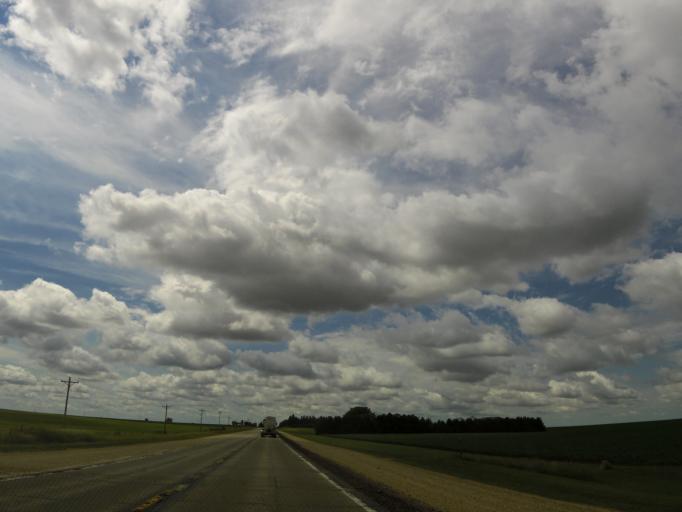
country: US
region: Iowa
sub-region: Howard County
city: Cresco
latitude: 43.3053
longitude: -92.2988
